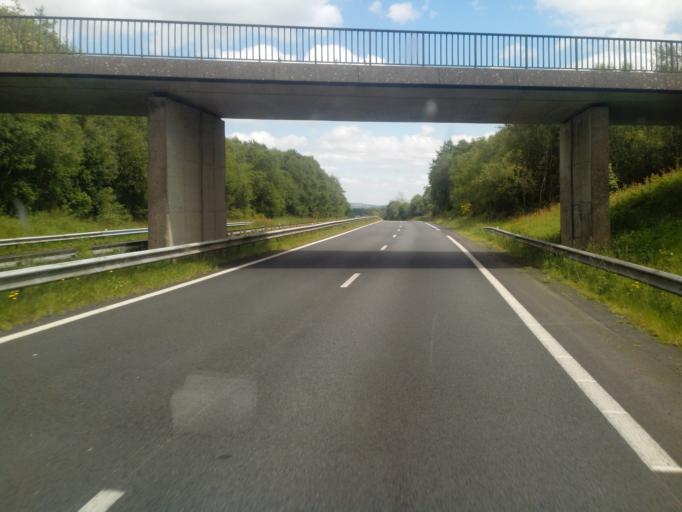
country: FR
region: Brittany
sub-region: Departement des Cotes-d'Armor
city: Plounevez-Moedec
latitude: 48.5510
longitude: -3.4664
